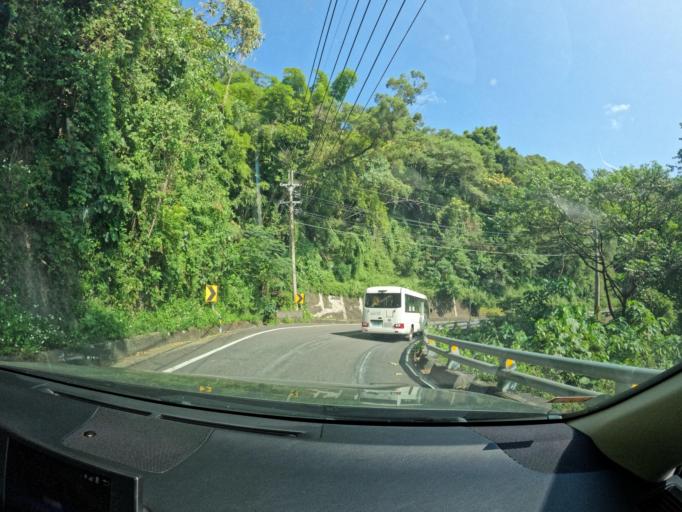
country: TW
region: Taiwan
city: Yujing
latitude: 23.0706
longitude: 120.6389
